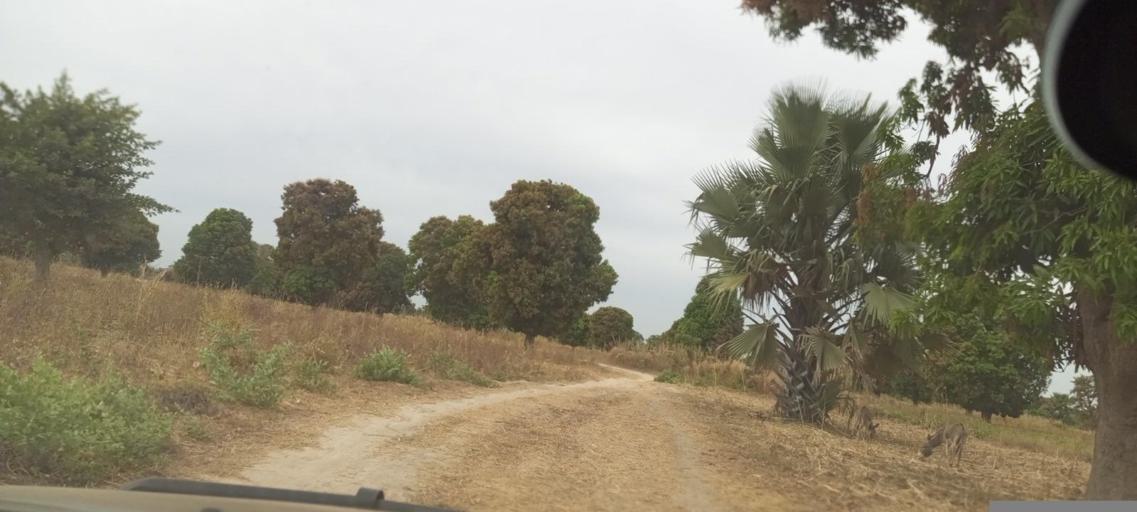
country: ML
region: Koulikoro
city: Kati
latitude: 12.7569
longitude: -8.3046
